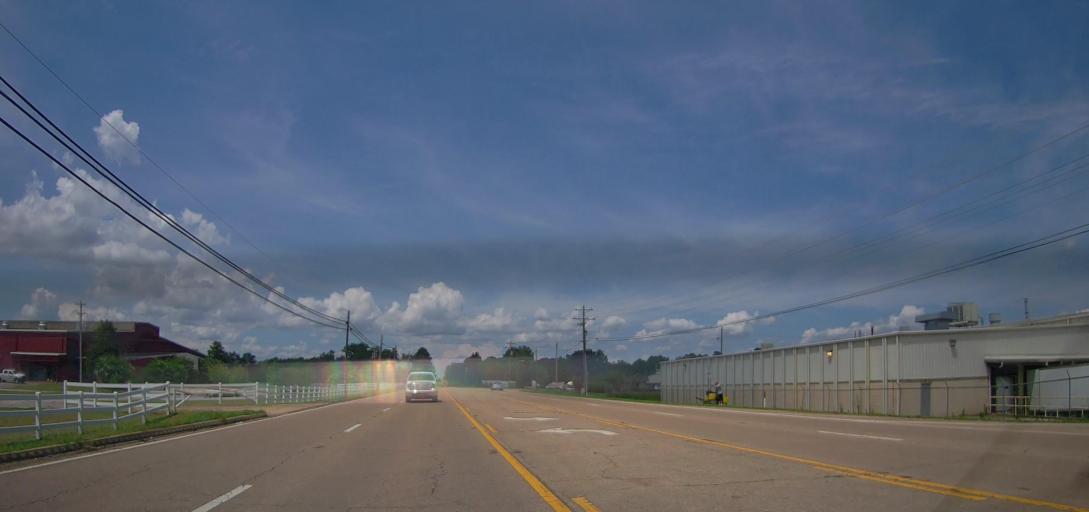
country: US
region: Mississippi
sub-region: Lee County
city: Verona
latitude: 34.1660
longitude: -88.7196
